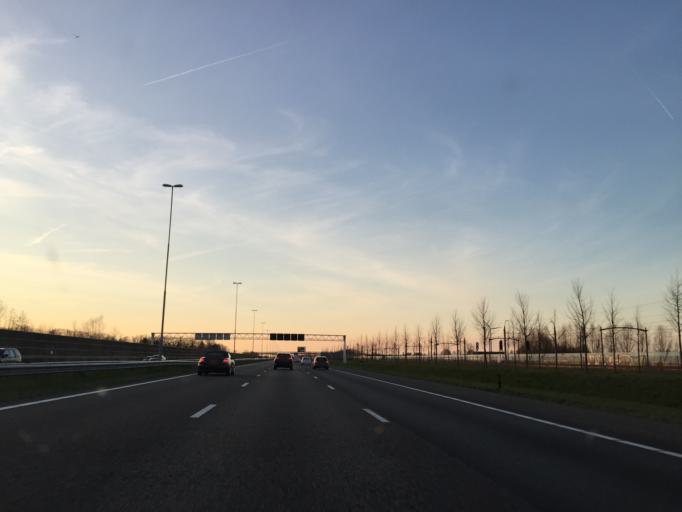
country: NL
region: North Brabant
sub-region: Gemeente Breda
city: Breda
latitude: 51.6203
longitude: 4.7102
